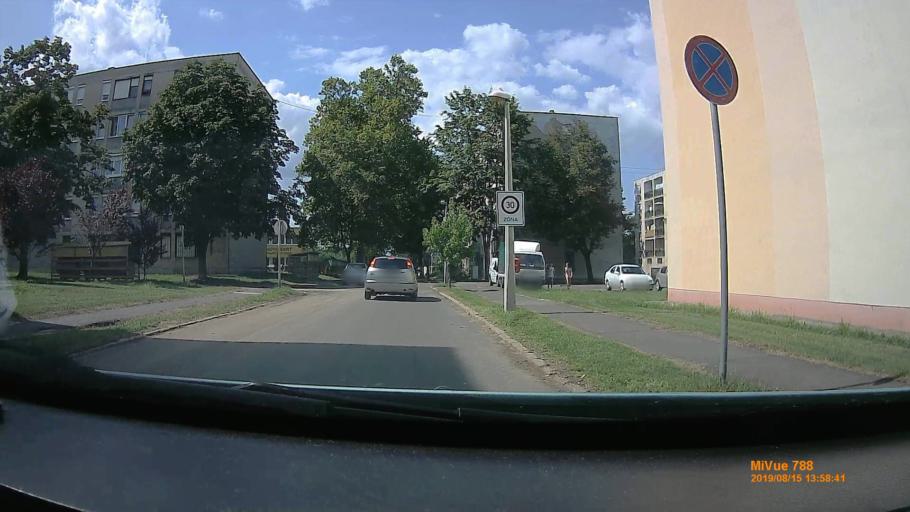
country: HU
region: Borsod-Abauj-Zemplen
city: Kazincbarcika
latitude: 48.2546
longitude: 20.6180
